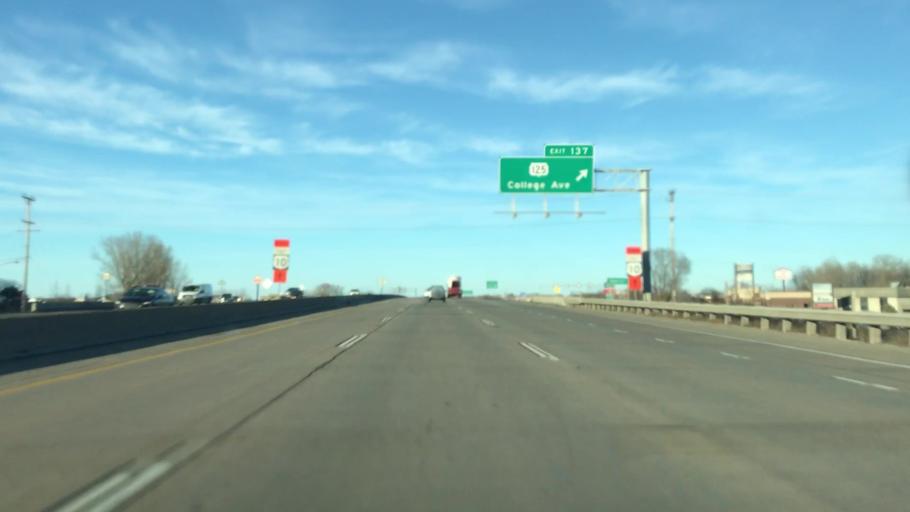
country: US
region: Wisconsin
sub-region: Outagamie County
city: Appleton
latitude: 44.2578
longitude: -88.4663
